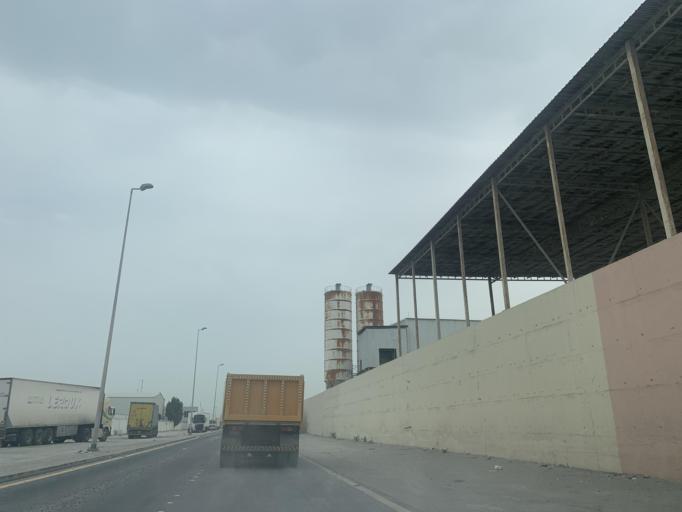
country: BH
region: Muharraq
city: Al Hadd
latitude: 26.2068
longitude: 50.6625
